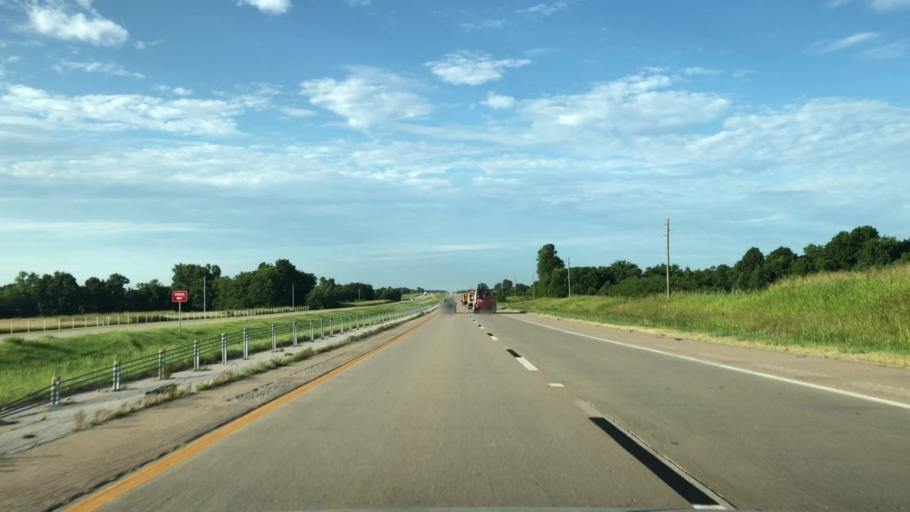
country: US
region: Oklahoma
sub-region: Osage County
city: Skiatook
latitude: 36.4734
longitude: -95.9207
